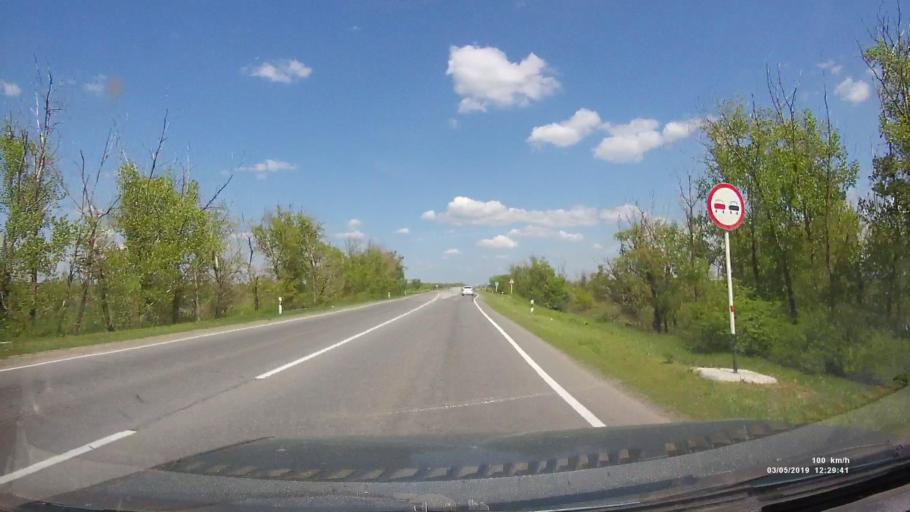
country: RU
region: Rostov
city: Semikarakorsk
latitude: 47.4911
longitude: 40.7375
